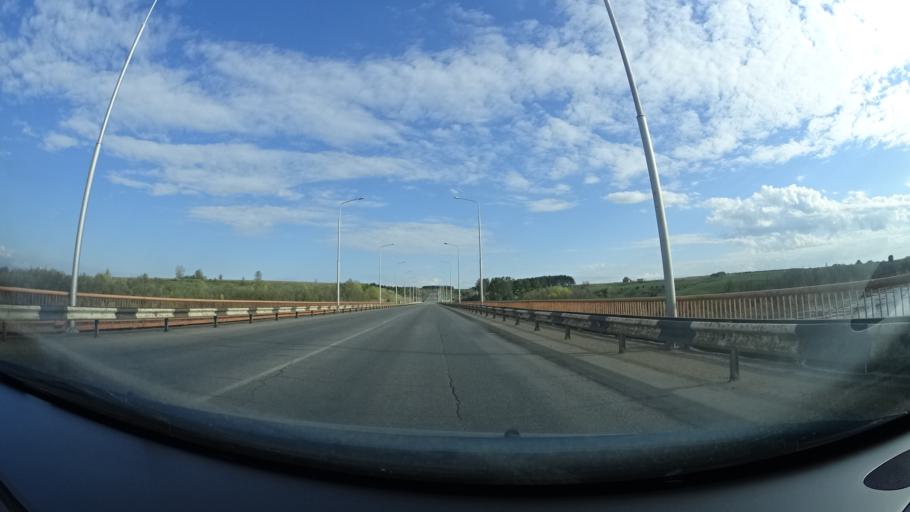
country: RU
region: Bashkortostan
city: Blagoveshchensk
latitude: 55.0694
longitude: 55.8079
